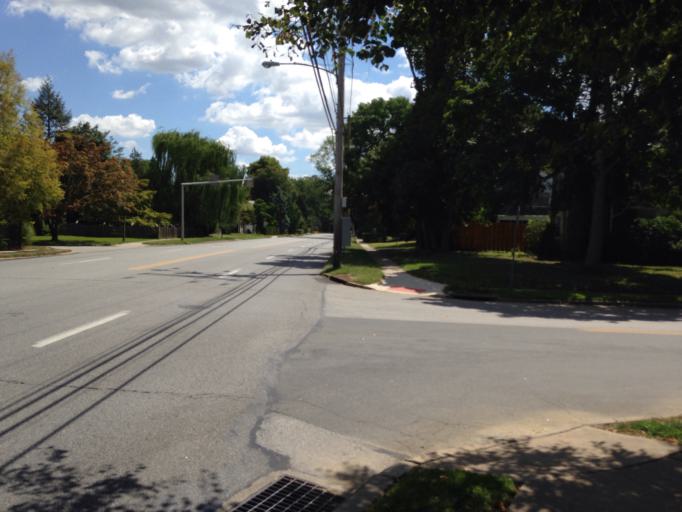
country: US
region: Pennsylvania
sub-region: Montgomery County
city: Penn Wynne
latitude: 39.9843
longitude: -75.2742
